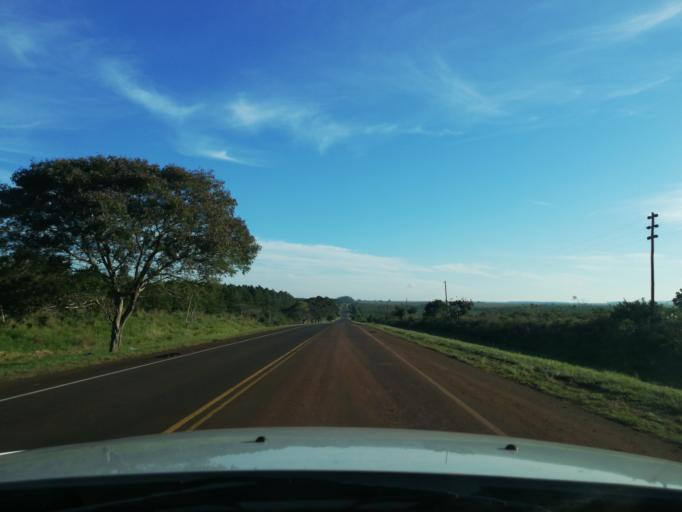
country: AR
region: Misiones
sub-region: Departamento de Capital
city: Posadas
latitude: -27.4258
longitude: -56.0001
